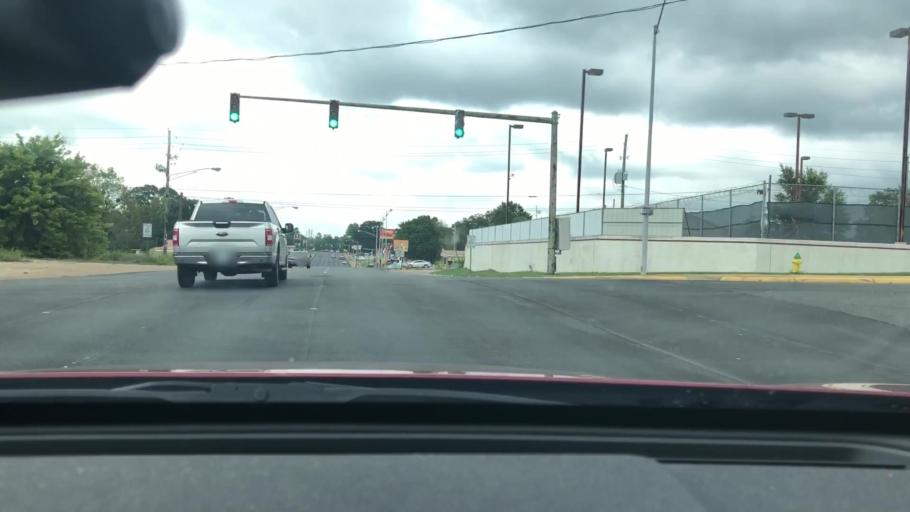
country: US
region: Texas
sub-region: Bowie County
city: Texarkana
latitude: 33.4280
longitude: -94.0413
